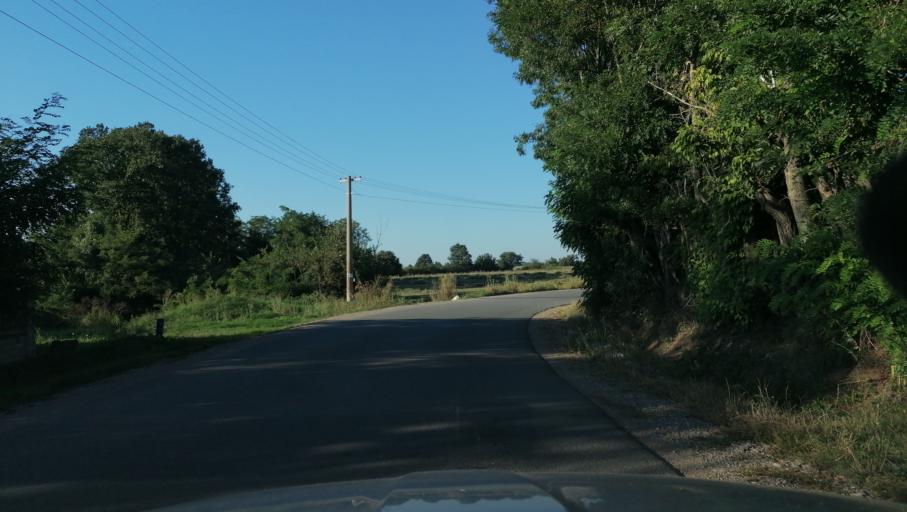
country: RS
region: Central Serbia
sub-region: Sumadijski Okrug
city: Kragujevac
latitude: 44.1123
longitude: 20.8361
